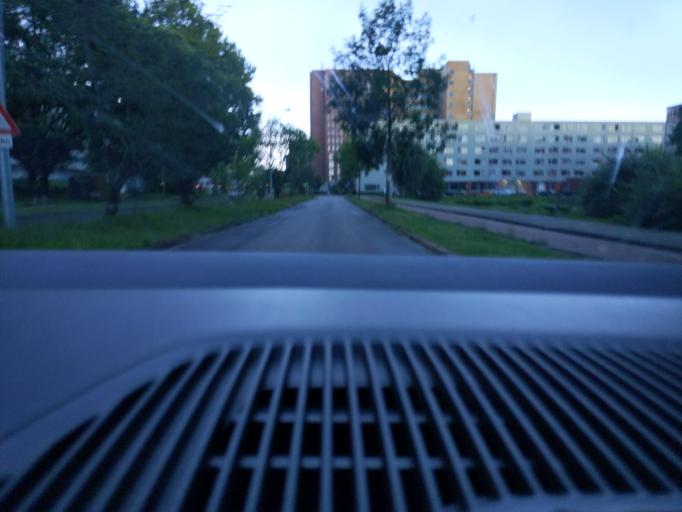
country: NL
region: Groningen
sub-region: Gemeente Groningen
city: Korrewegwijk
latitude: 53.2327
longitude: 6.5402
